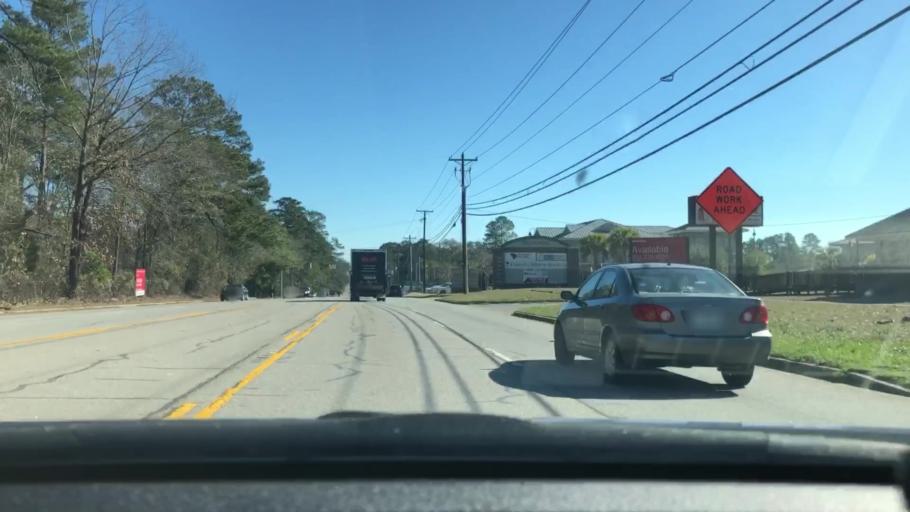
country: US
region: South Carolina
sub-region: Lexington County
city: Oak Grove
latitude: 34.0074
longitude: -81.1252
